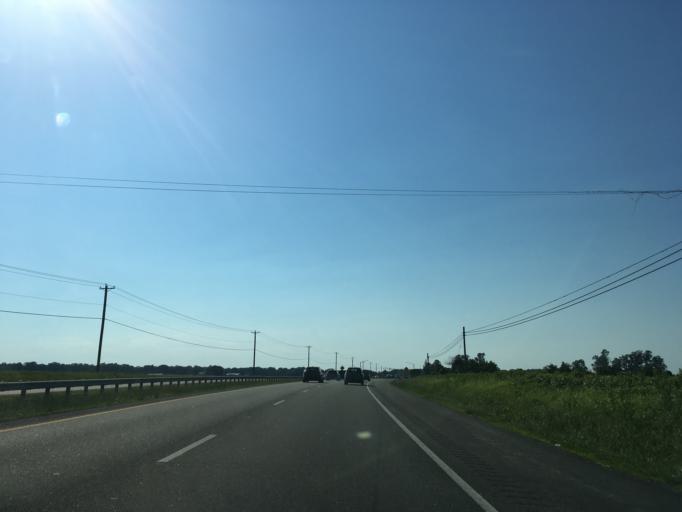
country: US
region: Maryland
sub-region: Queen Anne's County
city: Centreville
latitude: 38.9670
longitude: -76.1154
